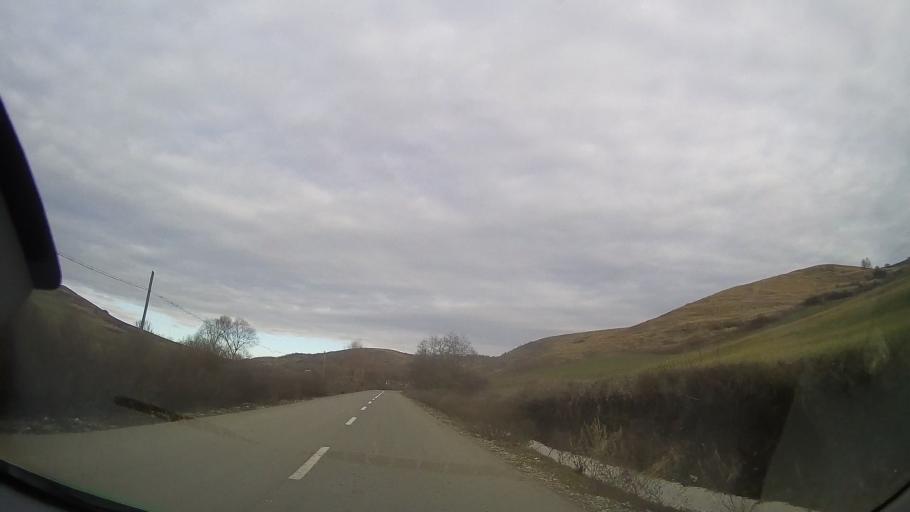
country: RO
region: Bistrita-Nasaud
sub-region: Comuna Silvasu de Campie
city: Silvasu de Campie
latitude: 46.8250
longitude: 24.3041
